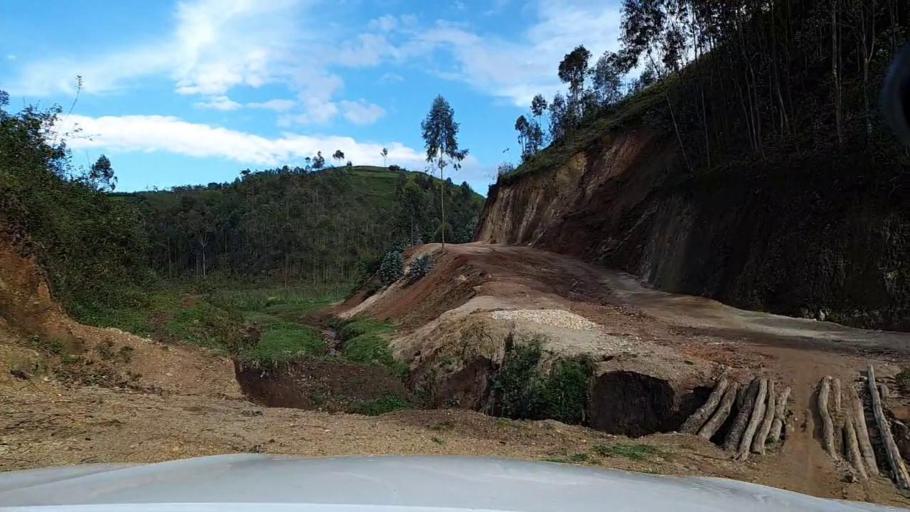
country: BI
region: Kayanza
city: Kayanza
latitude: -2.7812
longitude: 29.4527
